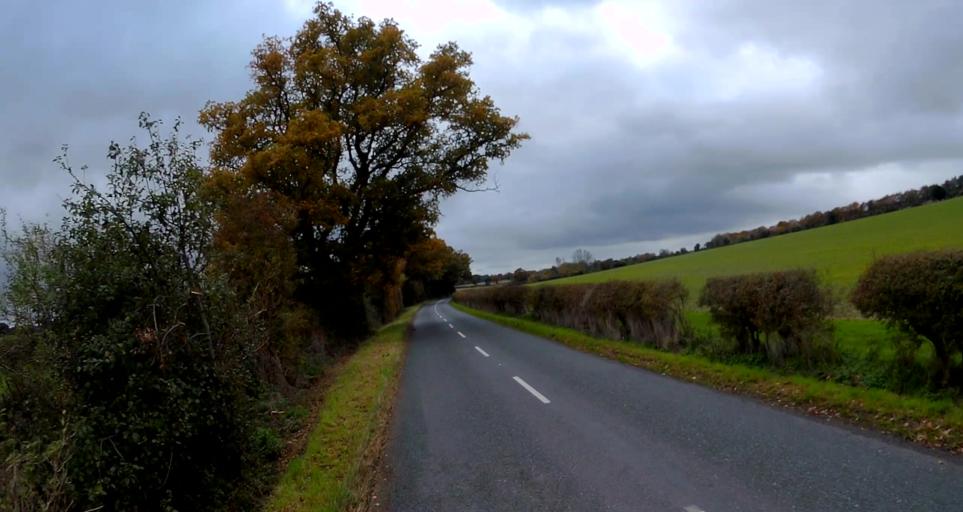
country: GB
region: England
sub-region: Hampshire
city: Four Marks
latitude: 51.1650
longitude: -1.1406
